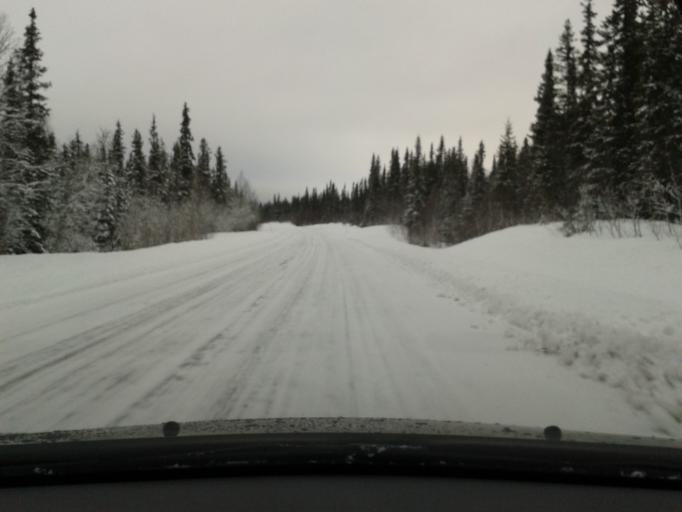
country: SE
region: Vaesterbotten
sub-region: Vilhelmina Kommun
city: Sjoberg
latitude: 65.0333
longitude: 15.8897
